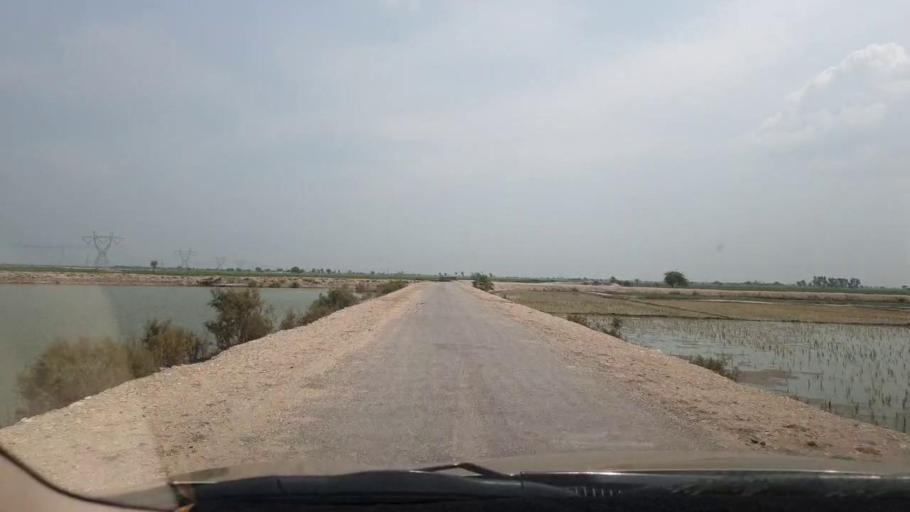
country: PK
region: Sindh
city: Goth Garelo
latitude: 27.5160
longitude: 68.1024
